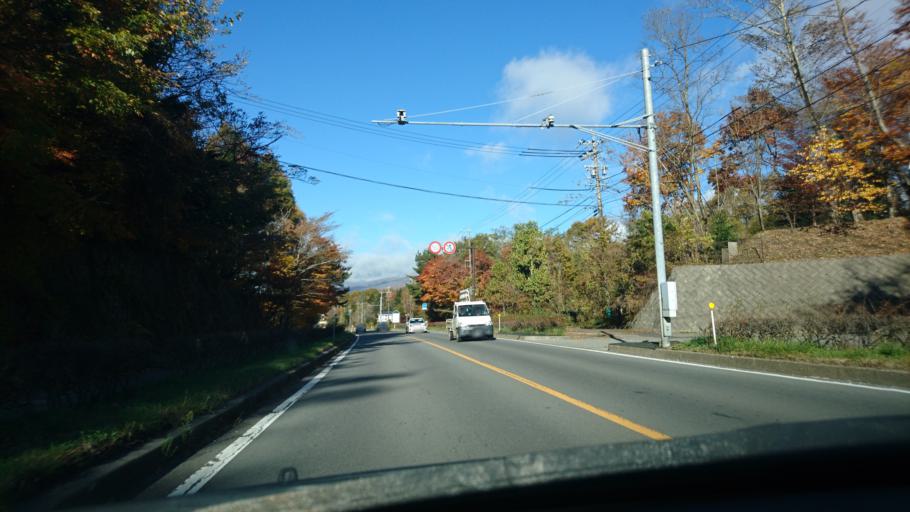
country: JP
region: Nagano
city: Saku
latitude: 36.3351
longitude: 138.6002
